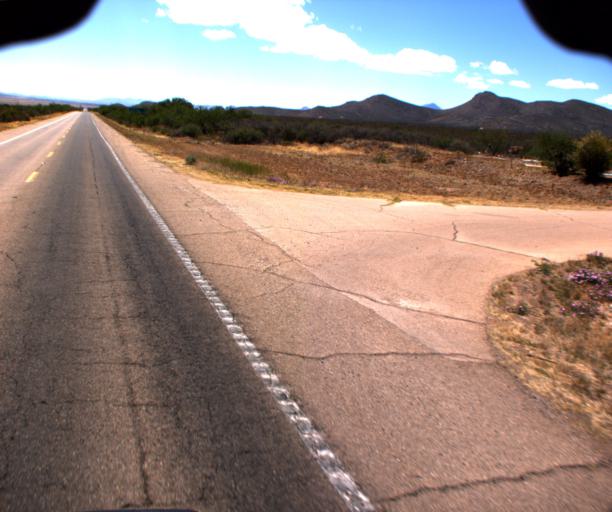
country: US
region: Arizona
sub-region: Cochise County
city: Bisbee
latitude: 31.3928
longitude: -109.9366
